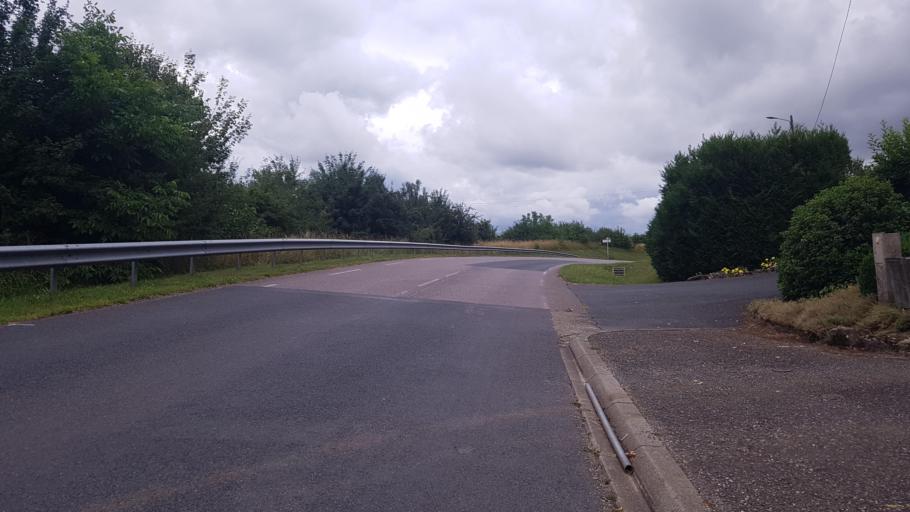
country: FR
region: Lorraine
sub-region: Departement de la Moselle
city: Lorquin
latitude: 48.7082
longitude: 6.9995
